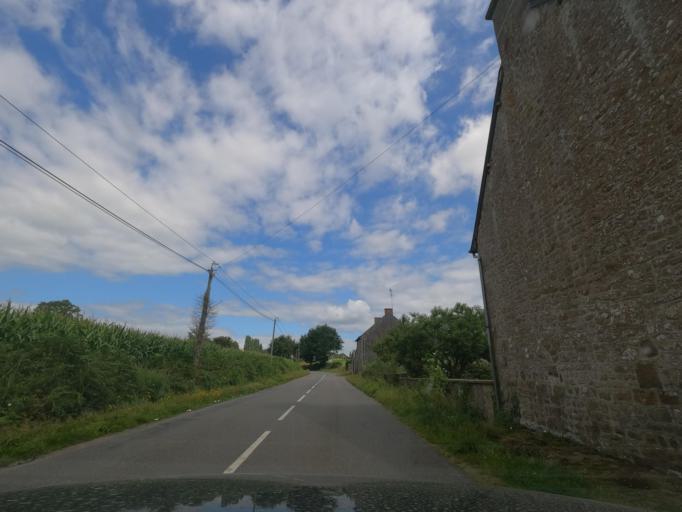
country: FR
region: Pays de la Loire
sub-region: Departement de la Mayenne
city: Landivy
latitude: 48.4458
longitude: -1.0741
